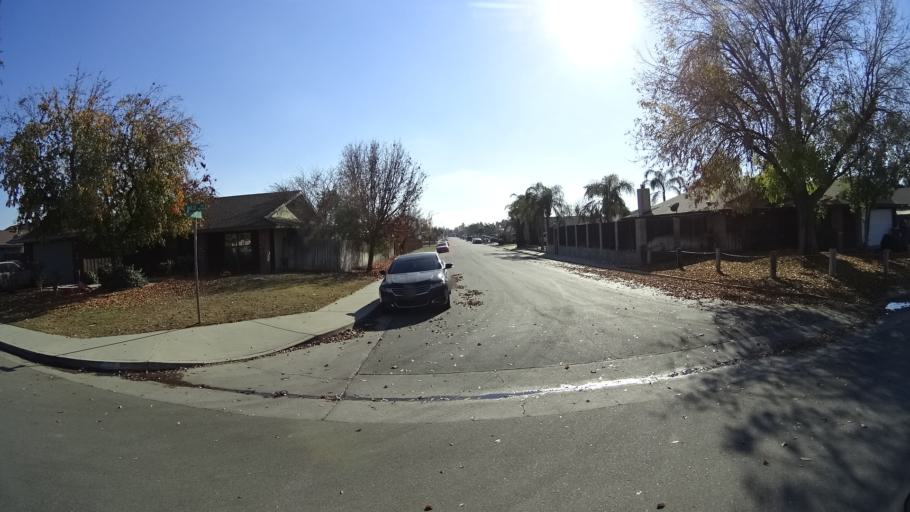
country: US
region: California
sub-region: Kern County
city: Greenfield
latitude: 35.3072
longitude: -119.0504
